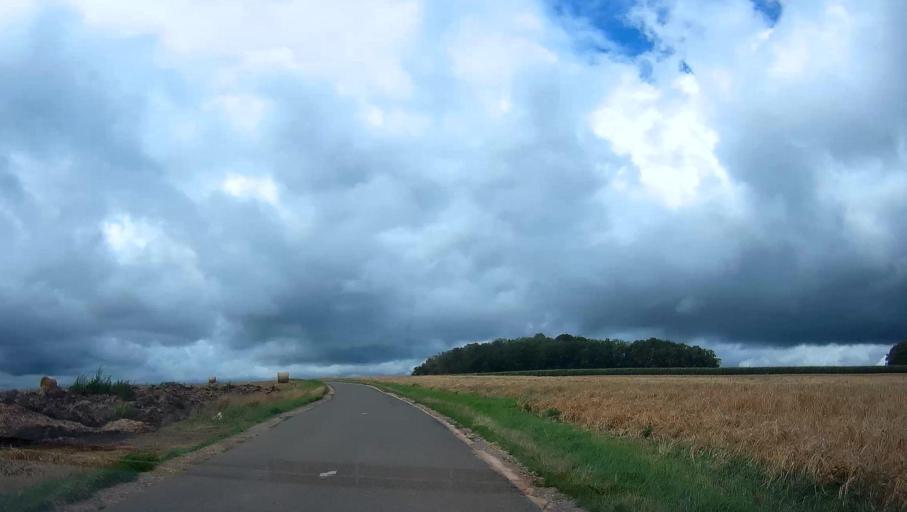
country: FR
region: Champagne-Ardenne
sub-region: Departement des Ardennes
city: Tournes
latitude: 49.7466
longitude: 4.5873
